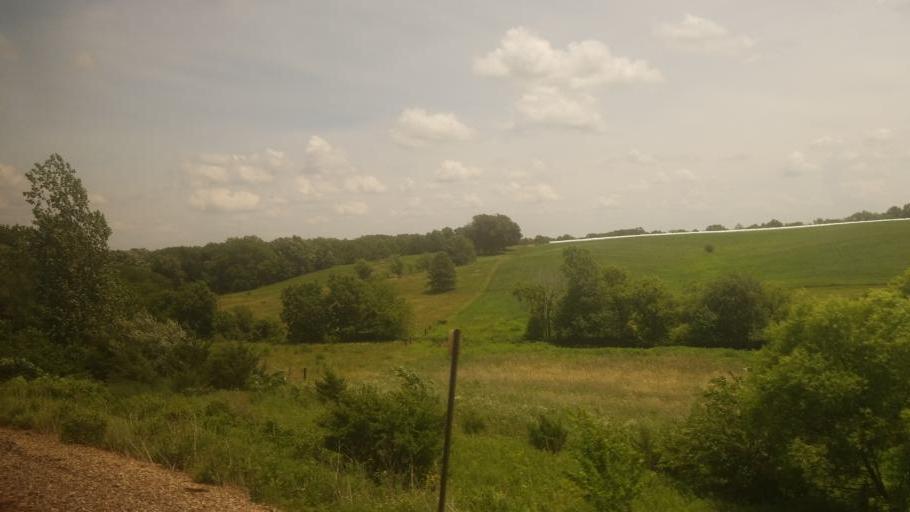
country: US
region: Missouri
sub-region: Macon County
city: La Plata
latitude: 40.0402
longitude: -92.4751
